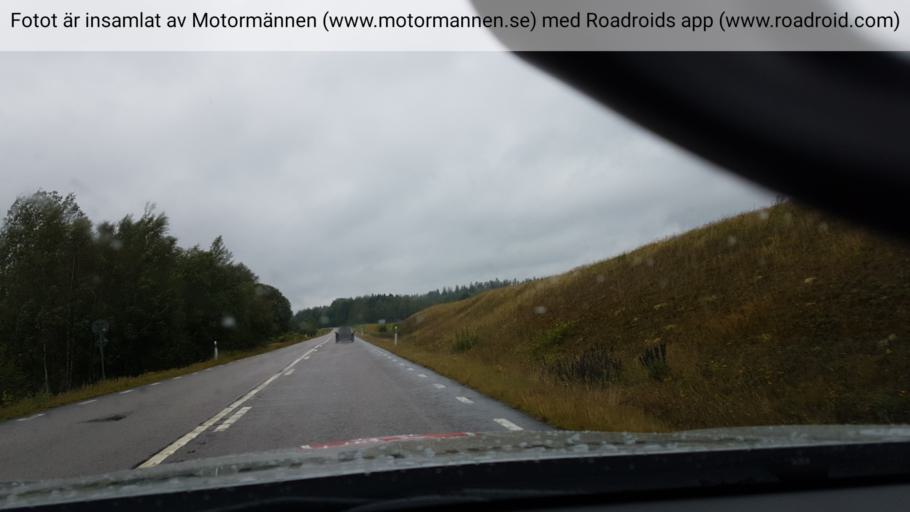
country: SE
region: Vaestra Goetaland
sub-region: Dals-Ed Kommun
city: Ed
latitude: 58.8786
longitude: 11.8934
